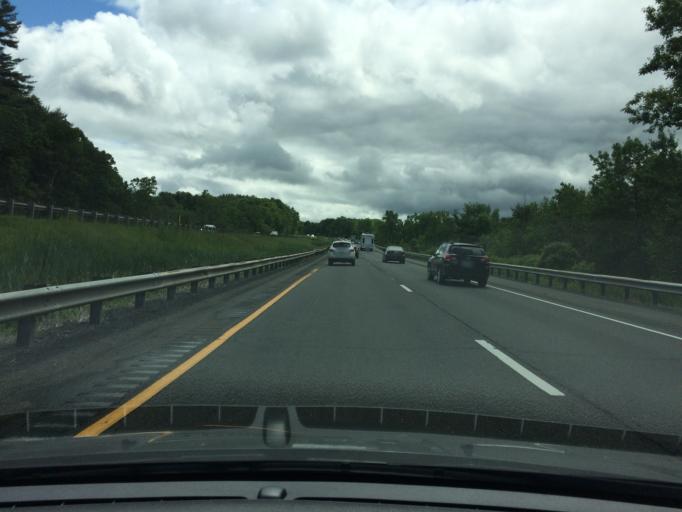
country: US
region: Massachusetts
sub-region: Berkshire County
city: Otis
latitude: 42.2638
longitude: -73.1285
